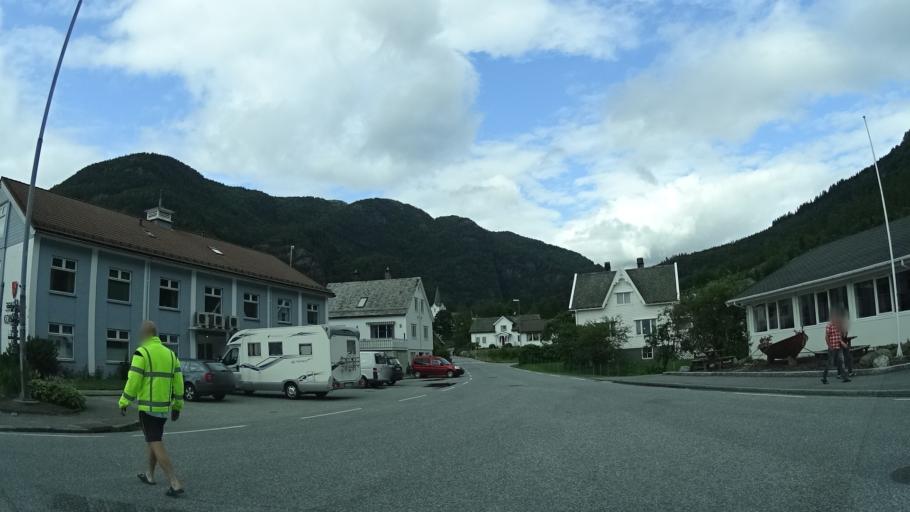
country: NO
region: Hordaland
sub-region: Jondal
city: Jondal
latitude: 60.2759
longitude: 6.2525
